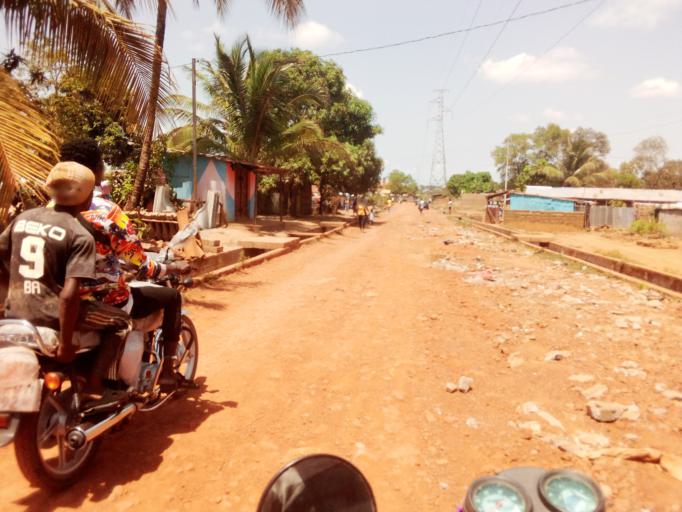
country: SL
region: Western Area
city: Waterloo
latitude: 8.3298
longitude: -13.0765
